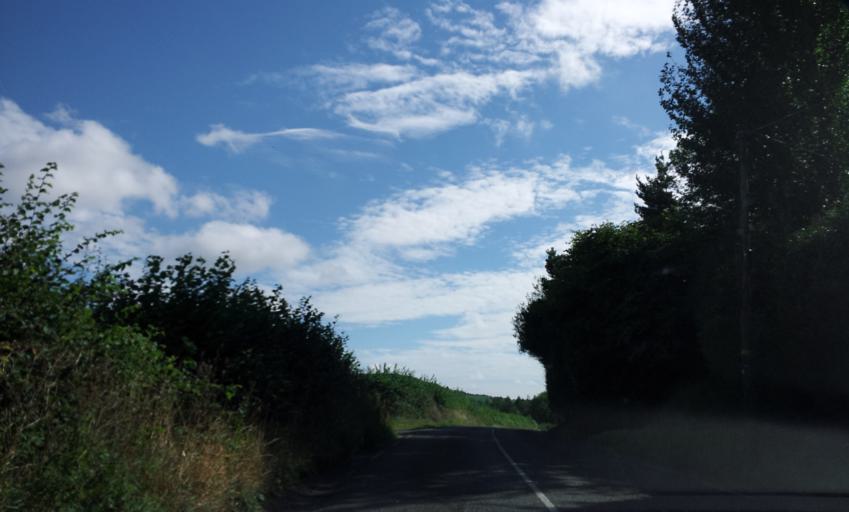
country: IE
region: Leinster
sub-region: Laois
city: Portlaoise
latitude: 53.0133
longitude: -7.2506
